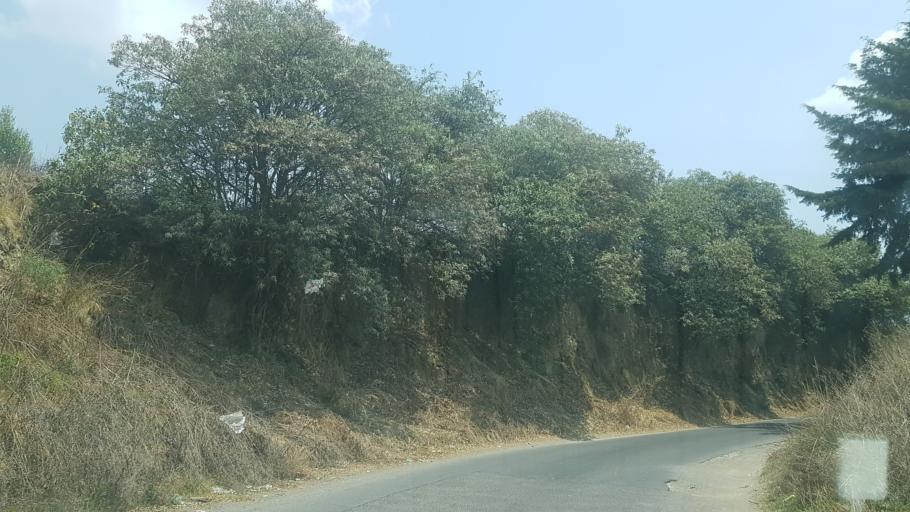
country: MX
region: Puebla
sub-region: San Nicolas de los Ranchos
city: San Pedro Yancuitlalpan
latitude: 19.0954
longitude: -98.4817
